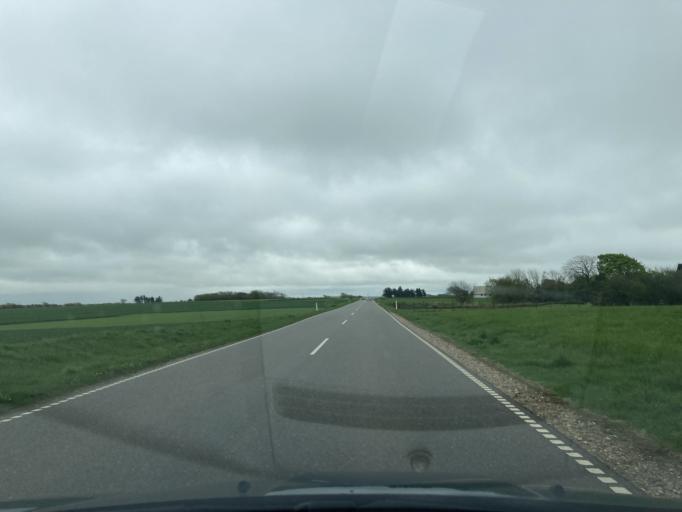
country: DK
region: North Denmark
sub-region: Thisted Kommune
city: Hurup
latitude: 56.8389
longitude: 8.3615
